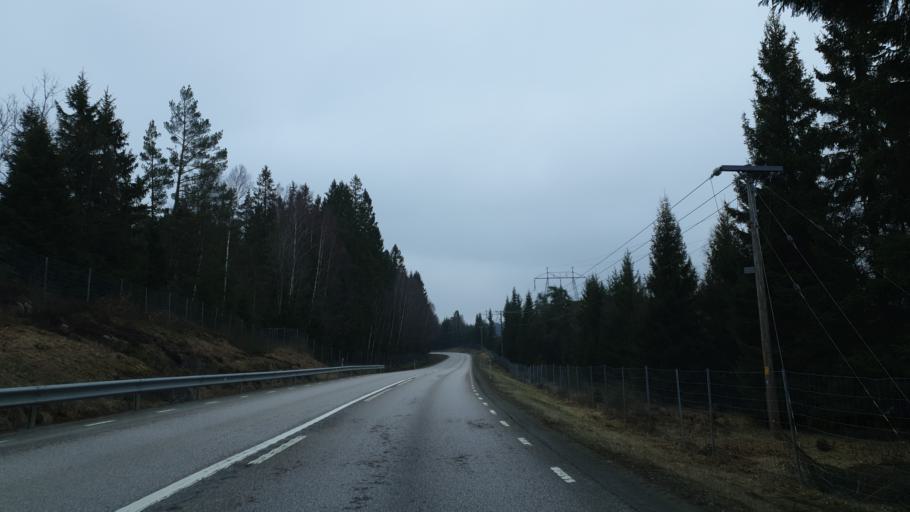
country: SE
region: Vaestra Goetaland
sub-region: Harryda Kommun
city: Hindas
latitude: 57.6421
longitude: 12.4053
